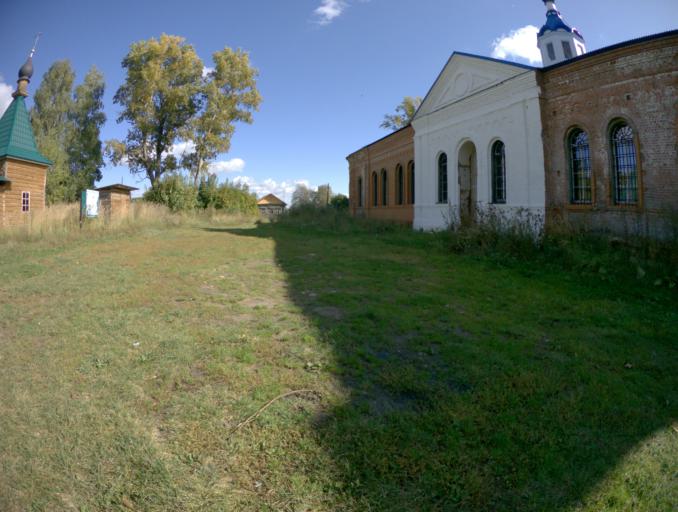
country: RU
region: Vladimir
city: Lakinsk
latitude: 55.8819
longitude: 39.8706
